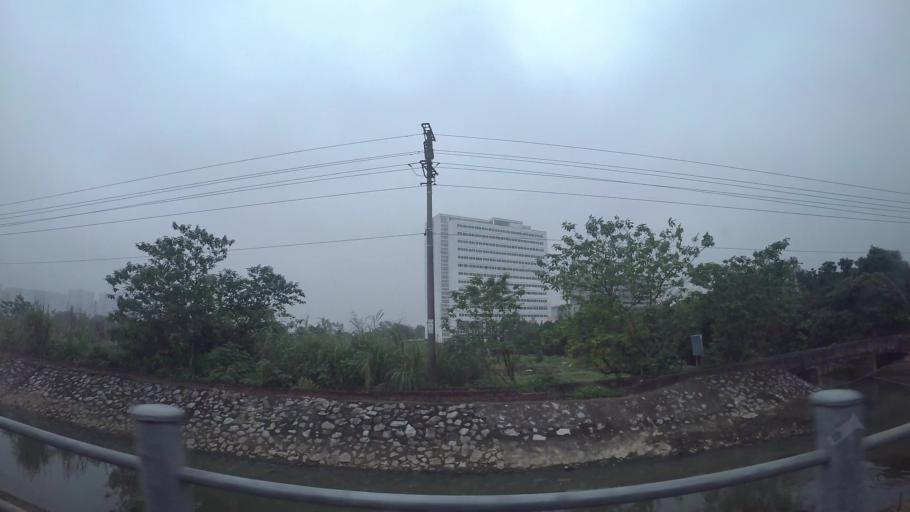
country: VN
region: Ha Noi
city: Van Dien
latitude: 20.9782
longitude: 105.8741
